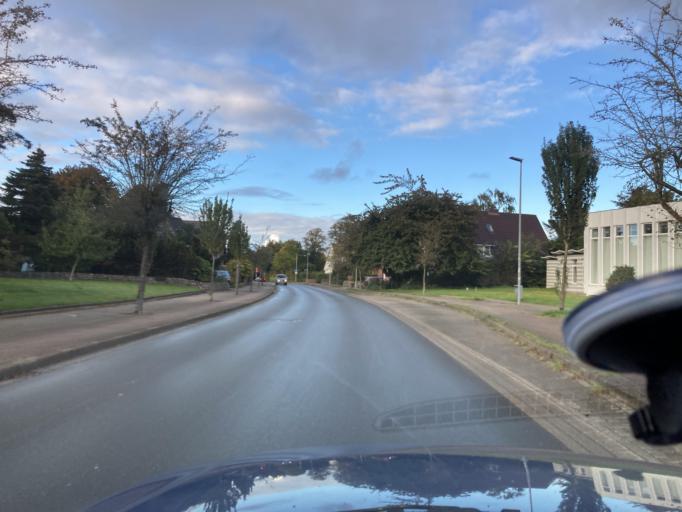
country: DE
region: Schleswig-Holstein
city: Heide
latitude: 54.2026
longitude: 9.1056
